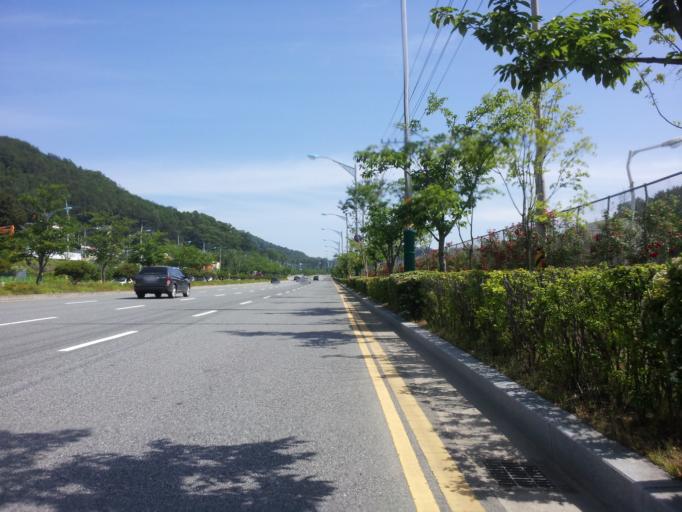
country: KR
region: Daejeon
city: Daejeon
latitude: 36.3232
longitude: 127.4726
